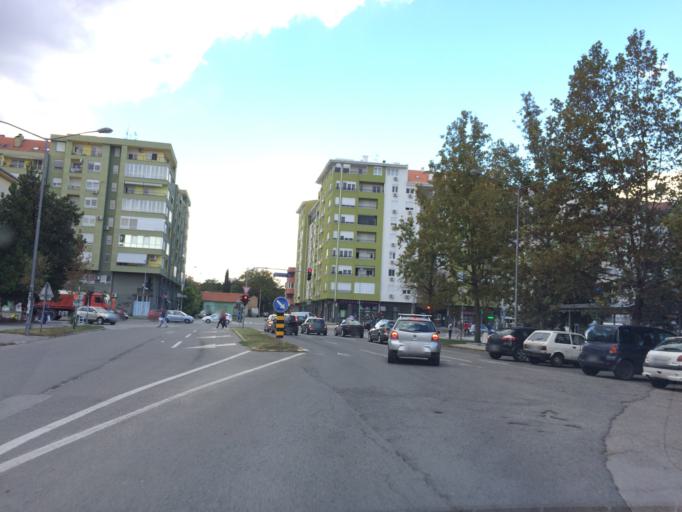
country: RS
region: Autonomna Pokrajina Vojvodina
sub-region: Juznobacki Okrug
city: Novi Sad
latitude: 45.2407
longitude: 19.8314
